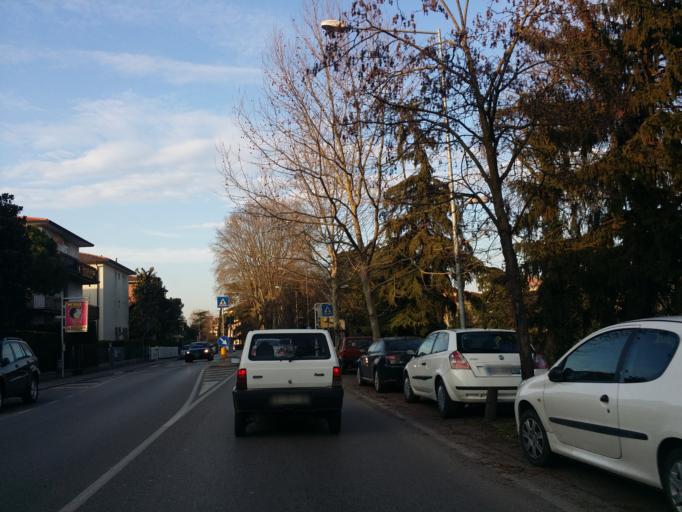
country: IT
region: Veneto
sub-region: Provincia di Padova
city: Padova
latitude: 45.4015
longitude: 11.8637
